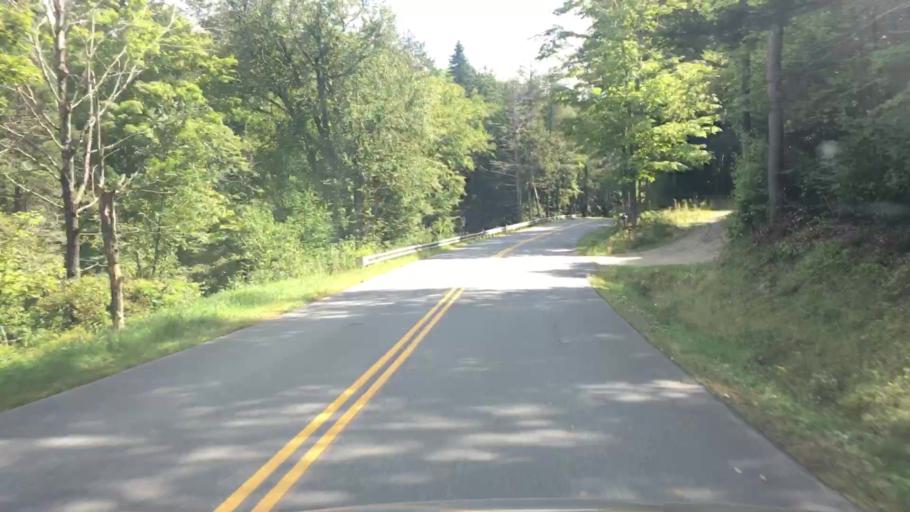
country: US
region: Vermont
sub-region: Windham County
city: Dover
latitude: 42.8175
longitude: -72.7547
